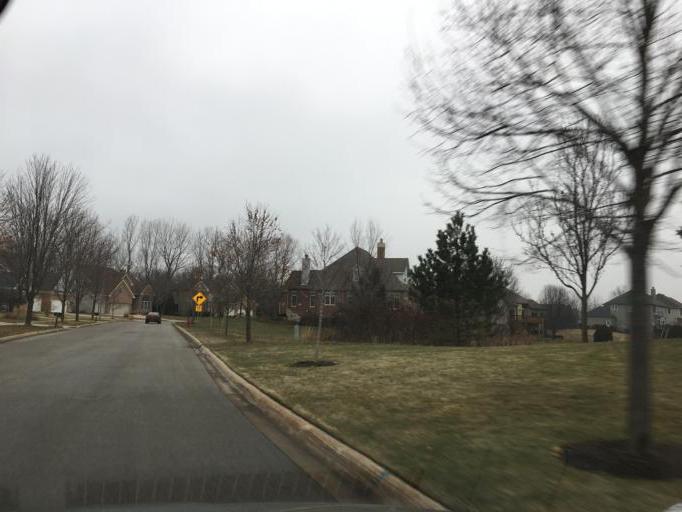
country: US
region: Illinois
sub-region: McHenry County
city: Lakewood
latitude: 42.2247
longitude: -88.3621
